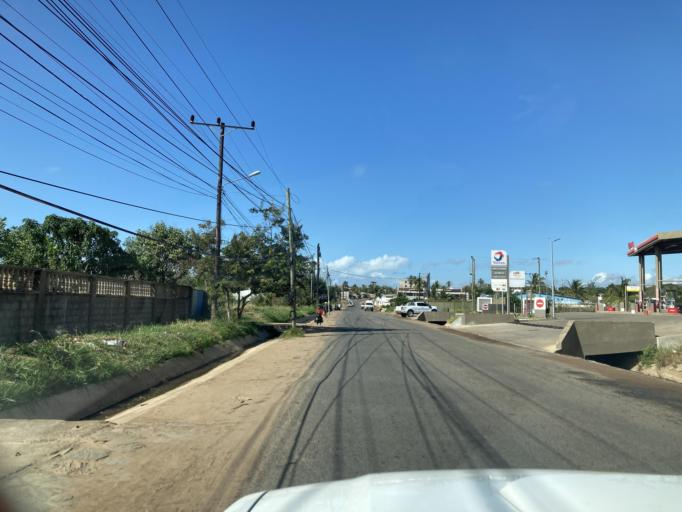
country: MZ
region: Cabo Delgado
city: Pemba
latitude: -12.9740
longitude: 40.5408
